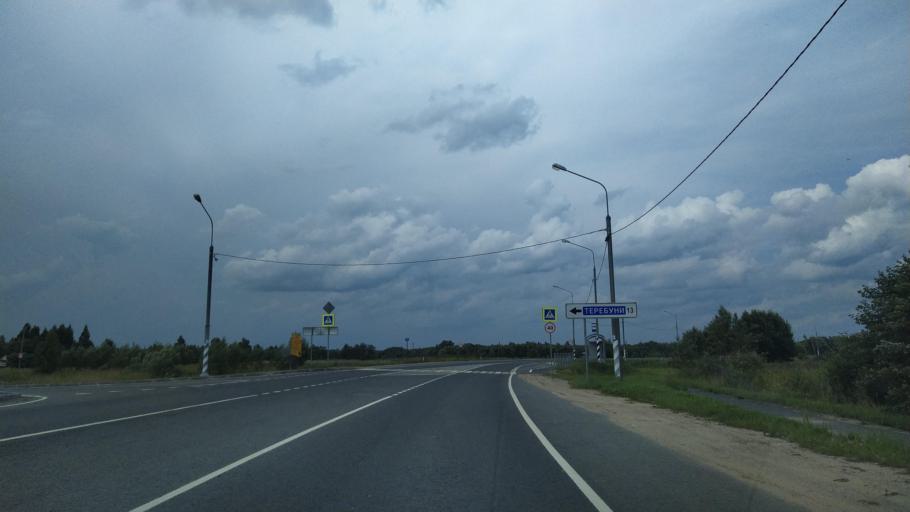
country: RU
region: Pskov
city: Dno
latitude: 58.0566
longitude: 29.9659
